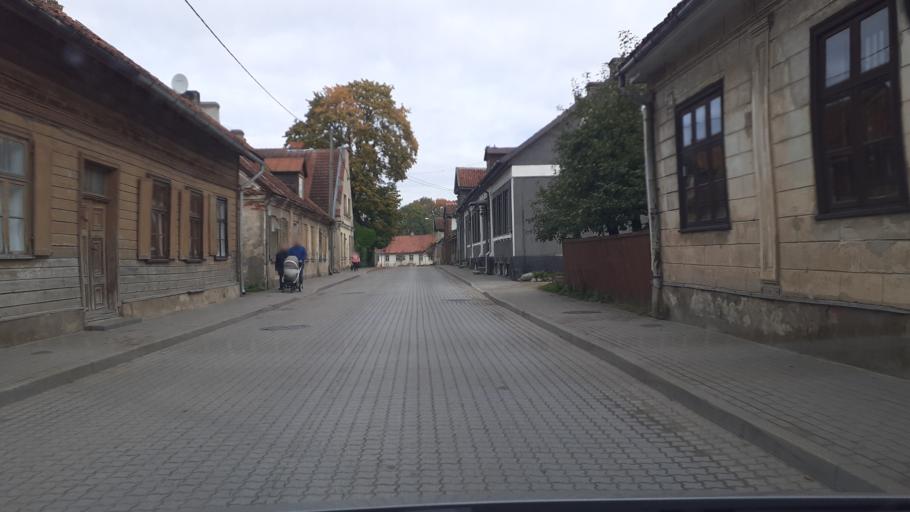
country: LV
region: Kuldigas Rajons
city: Kuldiga
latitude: 56.9637
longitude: 21.9719
